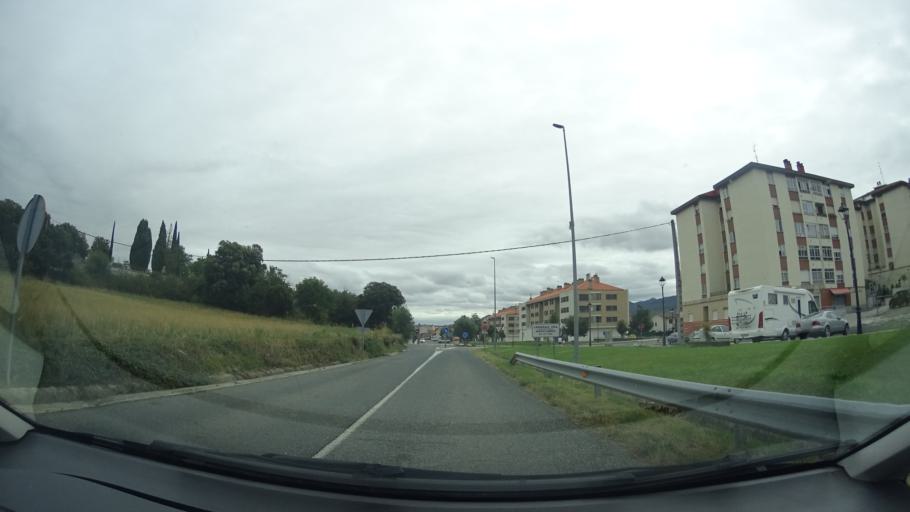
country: ES
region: Basque Country
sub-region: Provincia de Alava
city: Arminon
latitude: 42.8159
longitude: -2.8183
